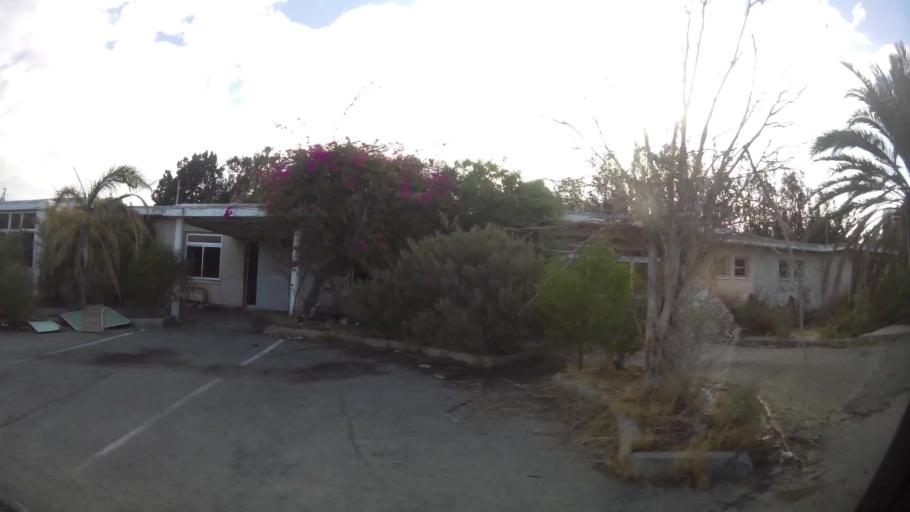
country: CY
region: Lefkosia
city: Nicosia
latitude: 35.1491
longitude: 33.3579
